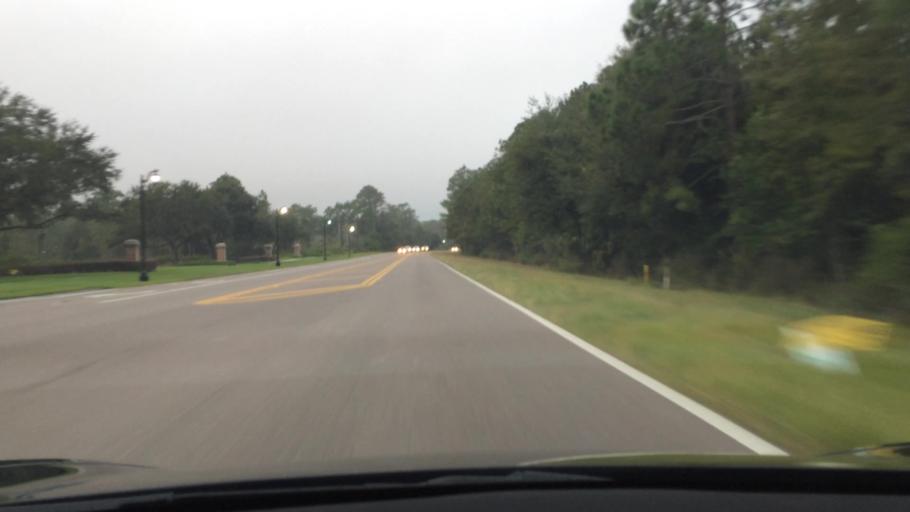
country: US
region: Florida
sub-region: Hillsborough County
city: Pebble Creek
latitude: 28.1704
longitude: -82.3772
